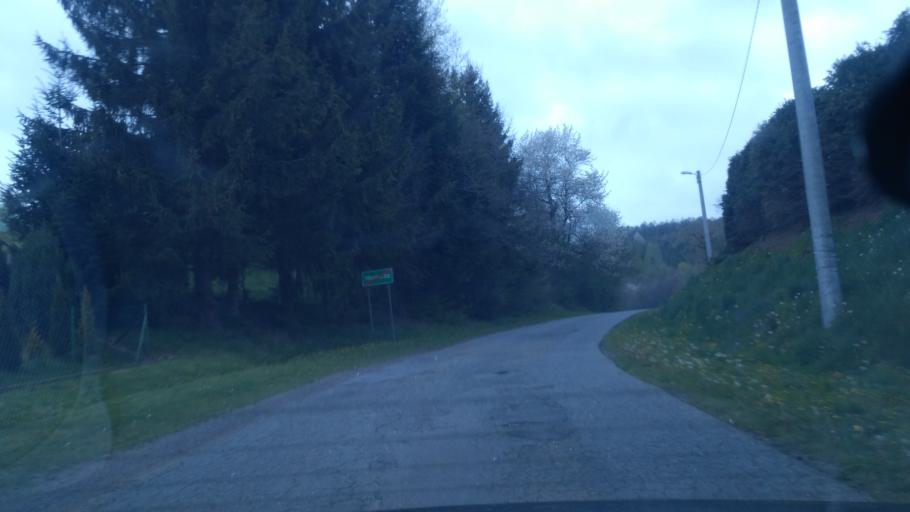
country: PL
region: Subcarpathian Voivodeship
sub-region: Powiat sanocki
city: Sanok
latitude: 49.6382
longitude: 22.2762
